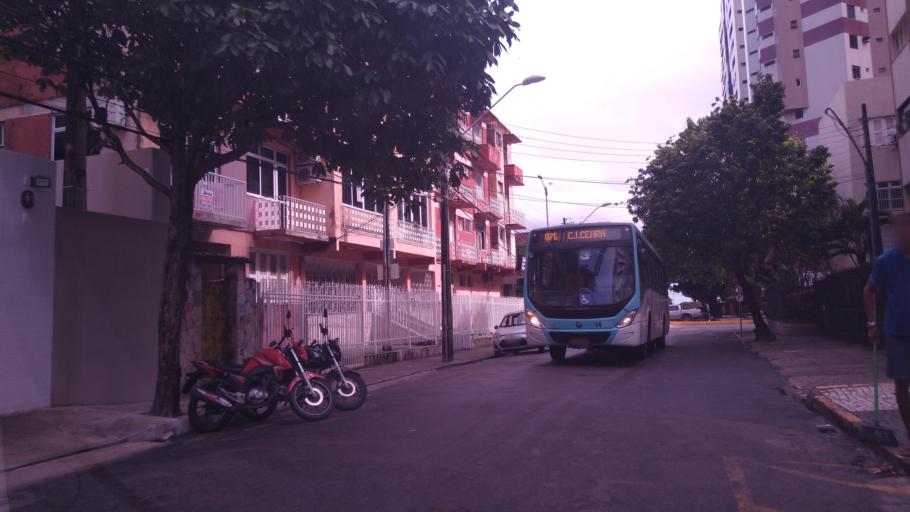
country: BR
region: Ceara
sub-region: Fortaleza
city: Fortaleza
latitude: -3.7271
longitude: -38.4902
